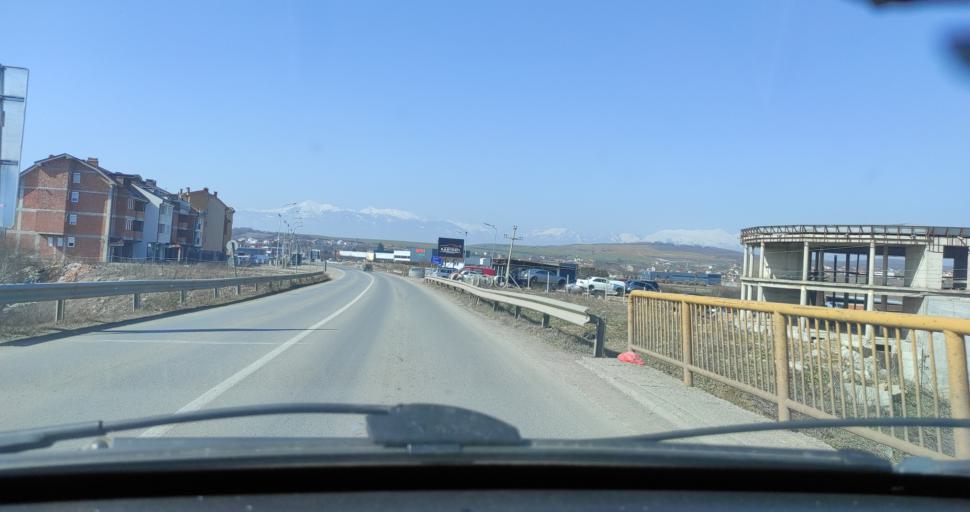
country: XK
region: Pec
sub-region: Komuna e Klines
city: Klina
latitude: 42.5929
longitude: 20.5748
